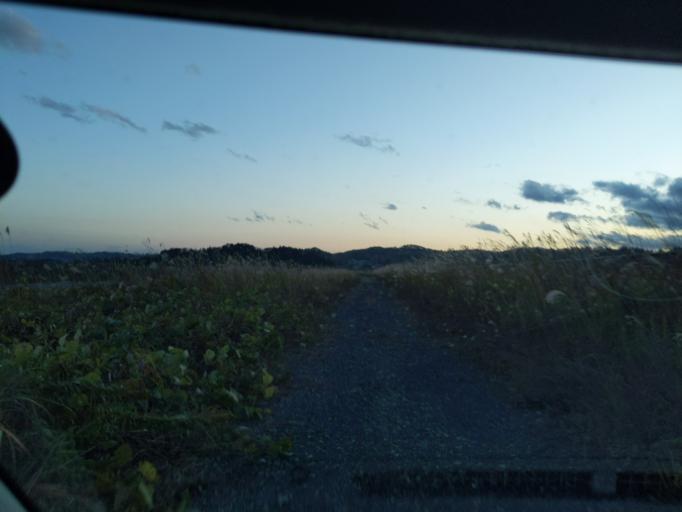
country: JP
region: Iwate
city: Ichinoseki
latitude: 39.0070
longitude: 141.1172
